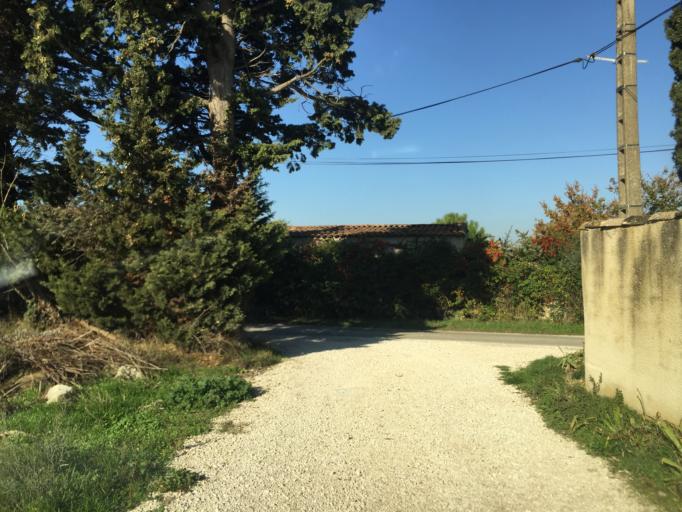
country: FR
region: Provence-Alpes-Cote d'Azur
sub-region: Departement du Vaucluse
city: Entraigues-sur-la-Sorgue
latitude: 44.0155
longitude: 4.9276
